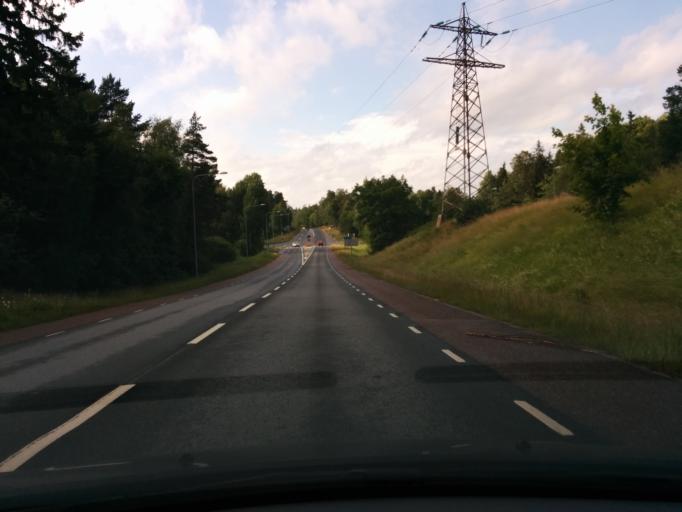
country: SE
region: Stockholm
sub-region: Sollentuna Kommun
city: Sollentuna
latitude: 59.4322
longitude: 17.9934
